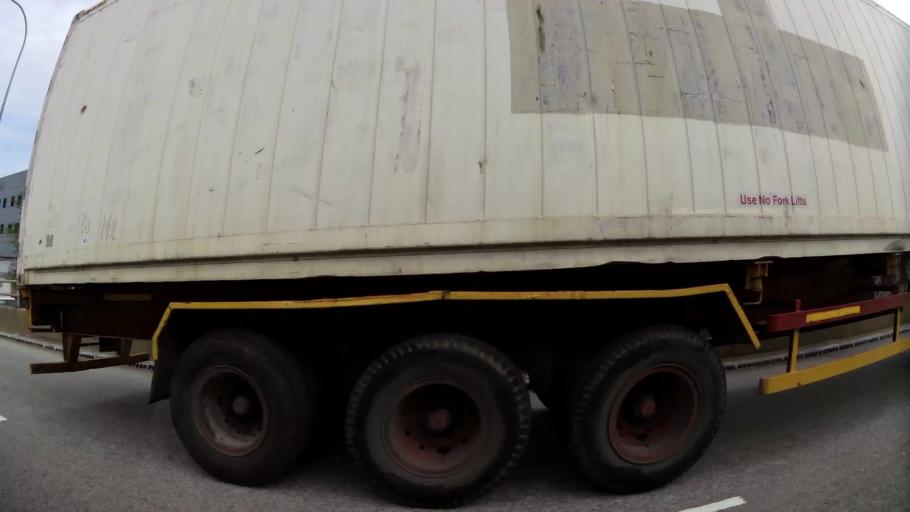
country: SG
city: Singapore
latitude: 1.3118
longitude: 103.7326
